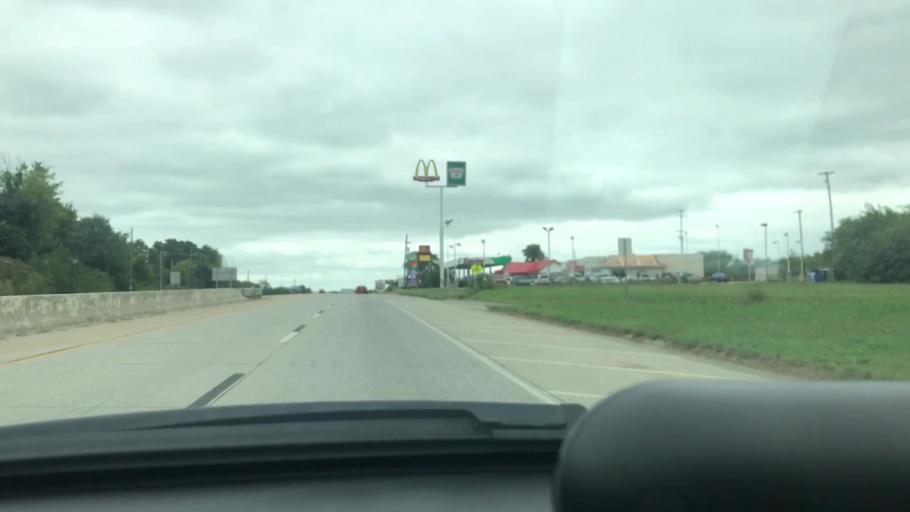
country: US
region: Oklahoma
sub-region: Mayes County
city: Chouteau
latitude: 36.1680
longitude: -95.3418
